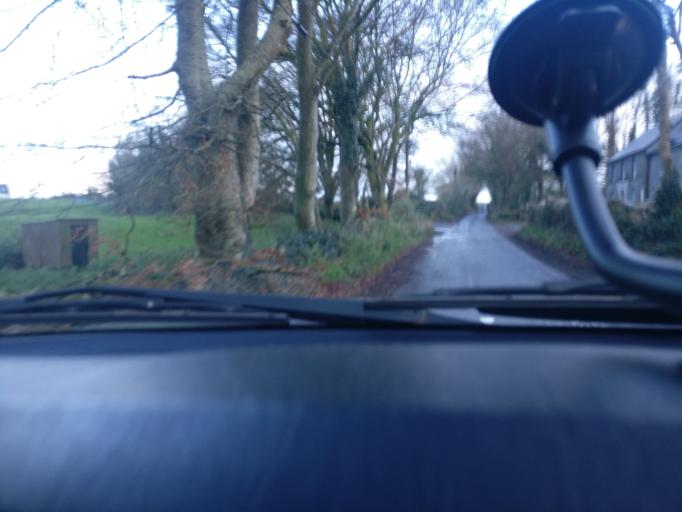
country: IE
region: Connaught
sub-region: County Galway
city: Athenry
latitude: 53.1984
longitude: -8.7015
